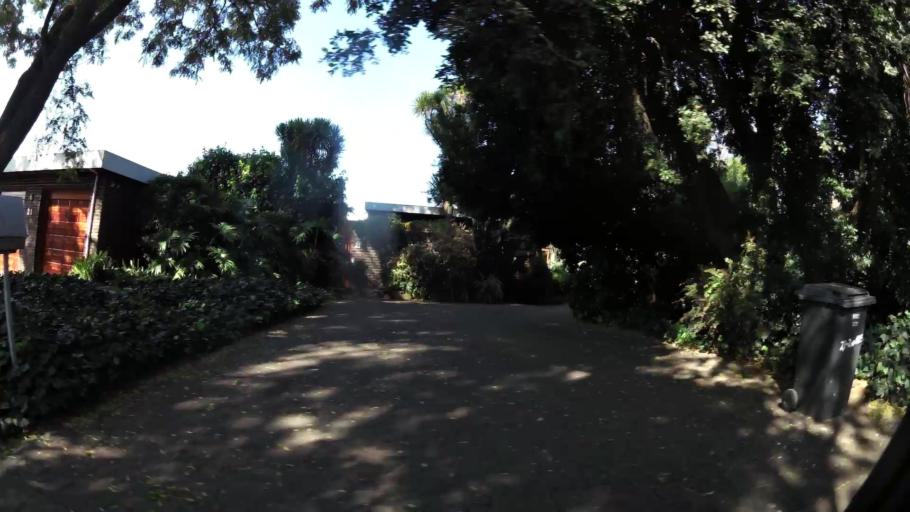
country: ZA
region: Gauteng
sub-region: City of Johannesburg Metropolitan Municipality
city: Roodepoort
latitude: -26.1064
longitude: 27.9709
